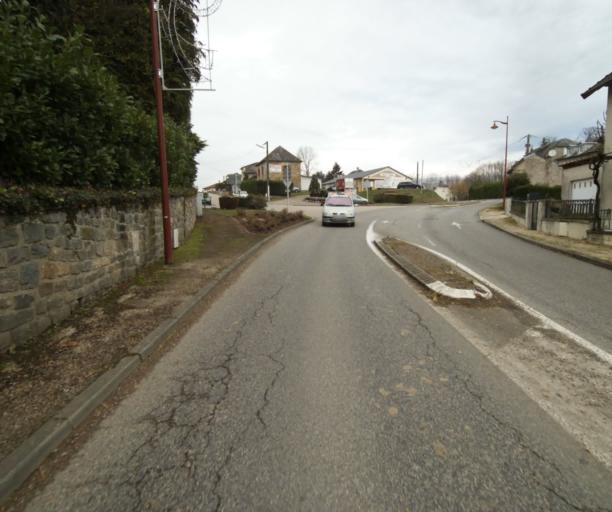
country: FR
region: Limousin
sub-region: Departement de la Correze
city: Chameyrat
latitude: 45.2655
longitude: 1.7233
